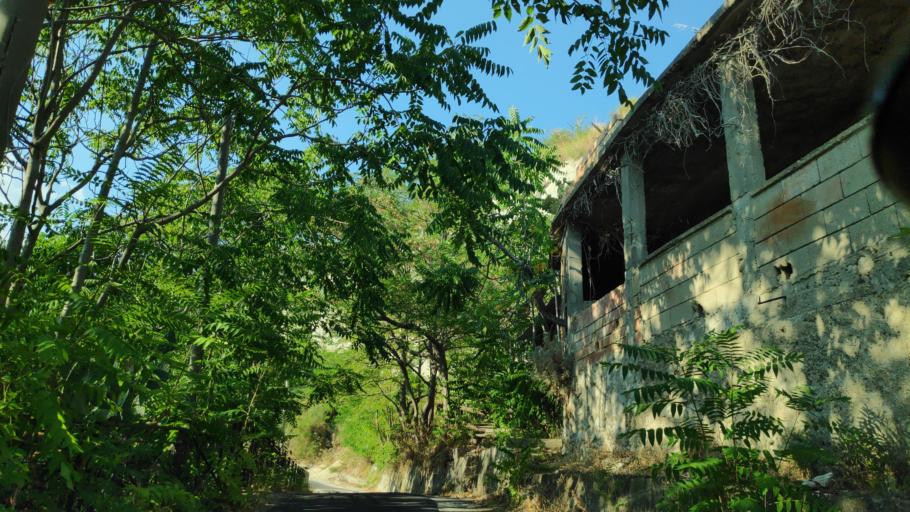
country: IT
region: Calabria
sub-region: Provincia di Catanzaro
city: Guardavalle
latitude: 38.5072
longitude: 16.5043
